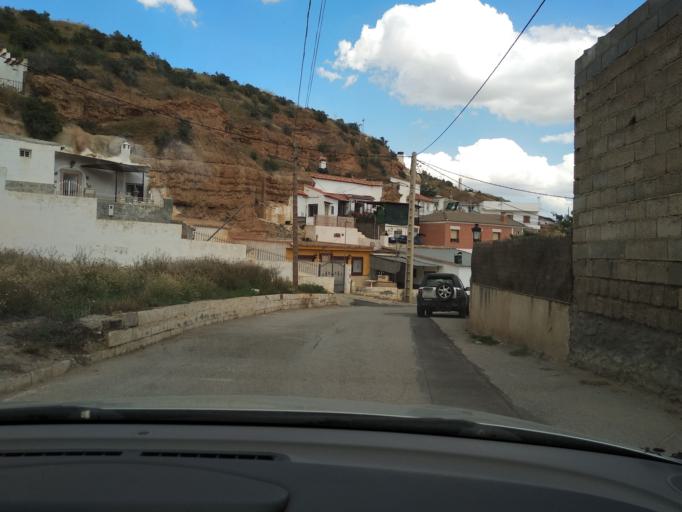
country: ES
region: Andalusia
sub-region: Provincia de Granada
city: Marchal
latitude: 37.2969
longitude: -3.2046
